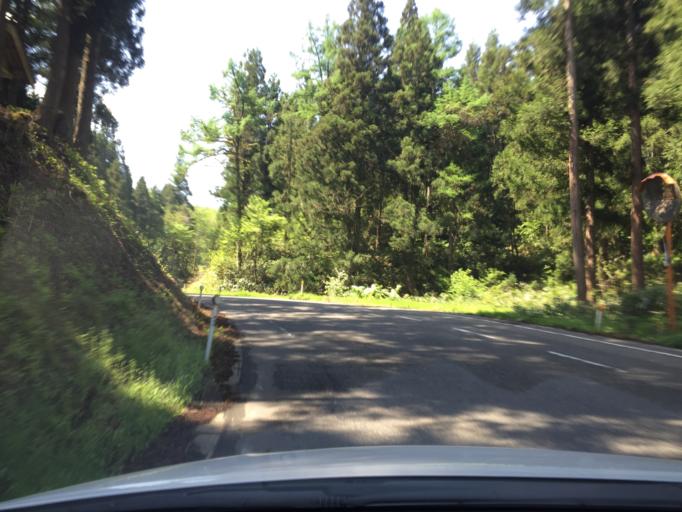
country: JP
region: Niigata
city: Kamo
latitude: 37.5741
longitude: 139.0858
